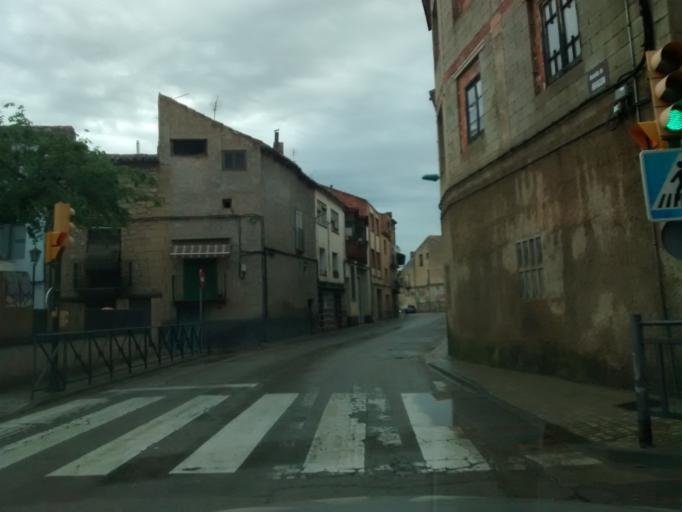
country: ES
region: Aragon
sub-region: Provincia de Zaragoza
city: Maella
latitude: 41.1214
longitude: 0.1369
